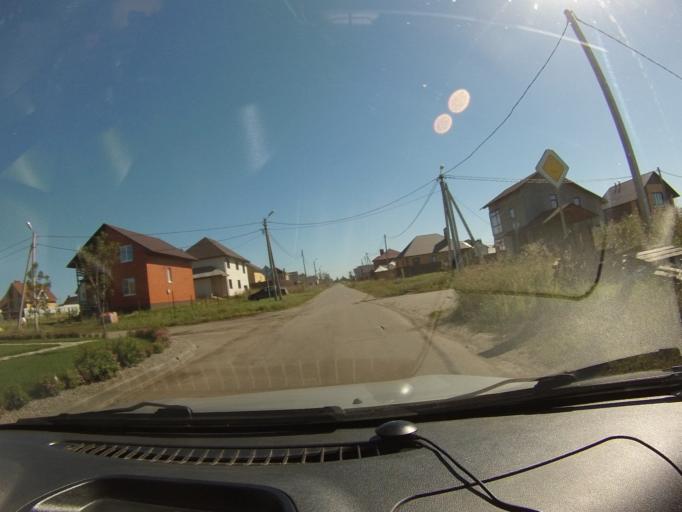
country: RU
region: Tambov
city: Komsomolets
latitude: 52.7726
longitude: 41.3585
